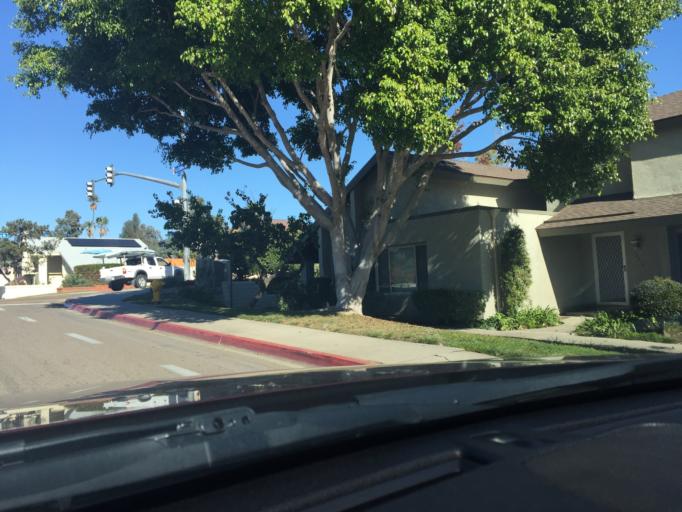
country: US
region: California
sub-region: San Diego County
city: La Mesa
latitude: 32.8266
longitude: -117.0959
